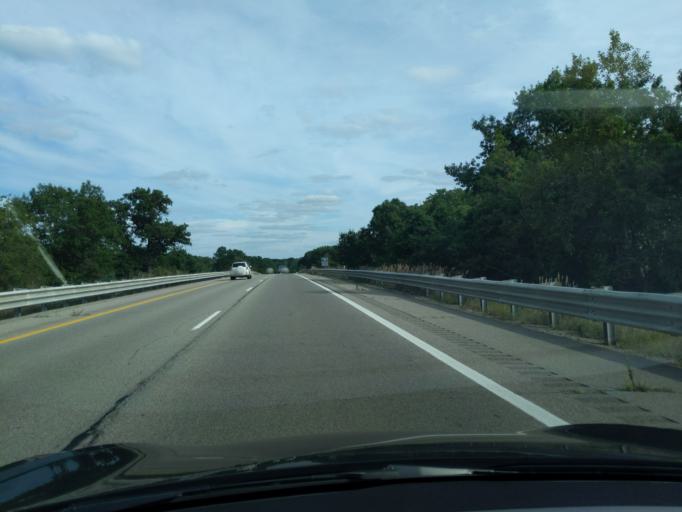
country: US
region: Michigan
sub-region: Muskegon County
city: Fruitport
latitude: 43.1385
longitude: -86.1563
